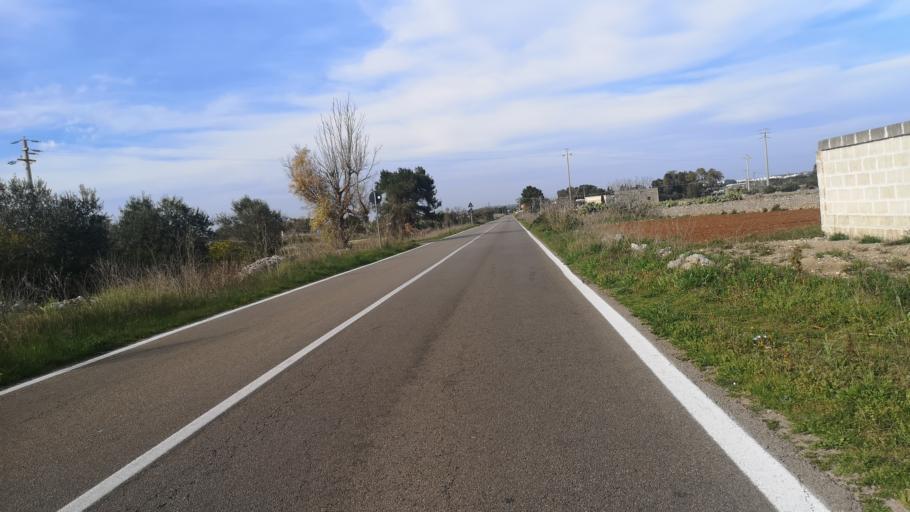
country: IT
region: Apulia
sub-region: Provincia di Lecce
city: Spongano
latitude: 40.0257
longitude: 18.3722
